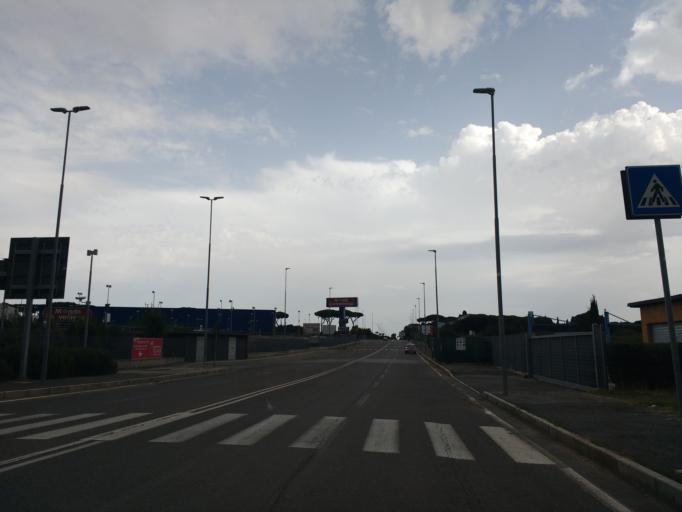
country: IT
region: Latium
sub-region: Citta metropolitana di Roma Capitale
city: Monte Migliore-La Selvotta
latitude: 41.7139
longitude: 12.4440
